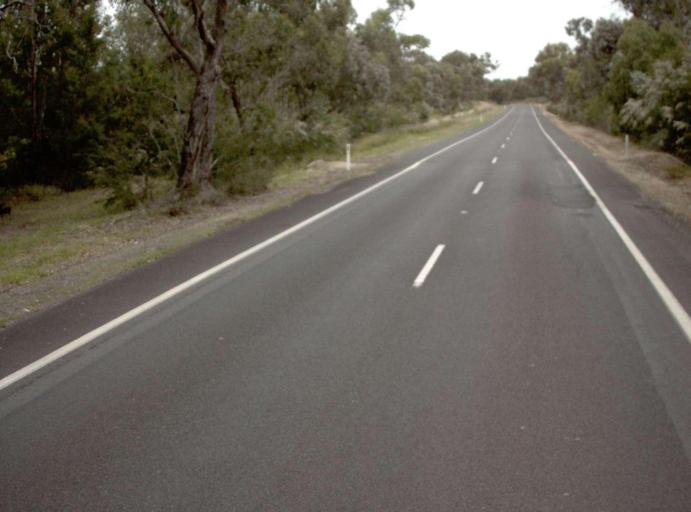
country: AU
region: Victoria
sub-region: Wellington
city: Sale
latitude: -38.3228
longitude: 147.0206
